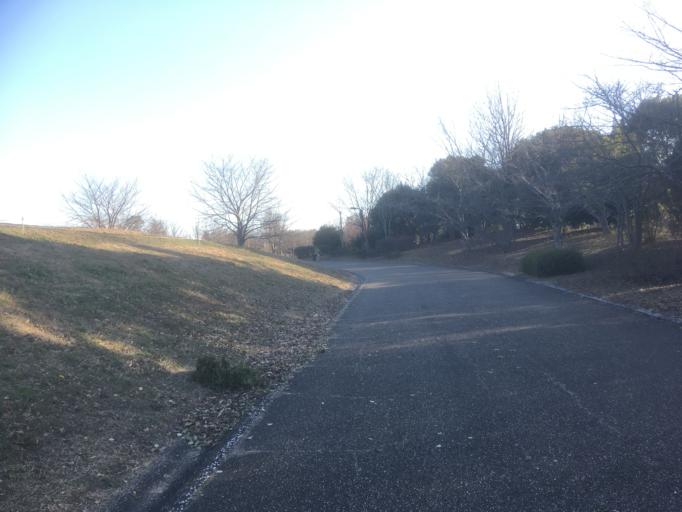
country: JP
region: Nara
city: Tawaramoto
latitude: 34.5680
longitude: 135.7373
